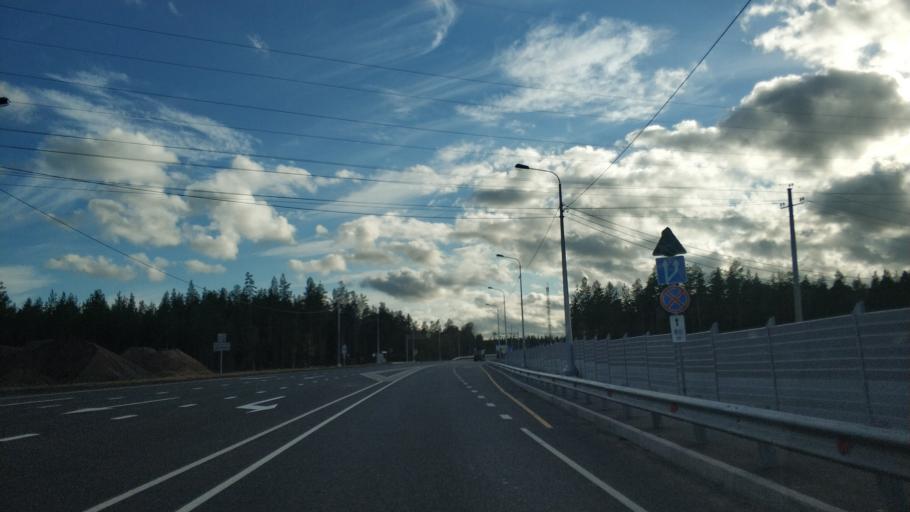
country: RU
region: Leningrad
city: Priozersk
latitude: 60.8472
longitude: 30.1443
